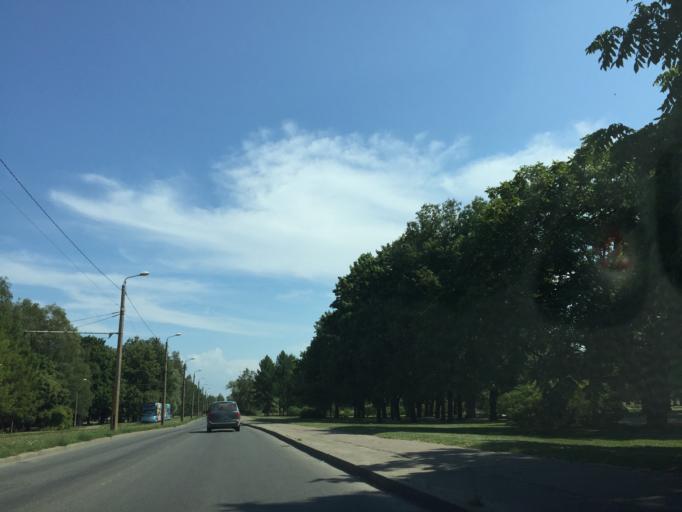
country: LV
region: Riga
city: Riga
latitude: 56.9416
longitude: 24.0836
